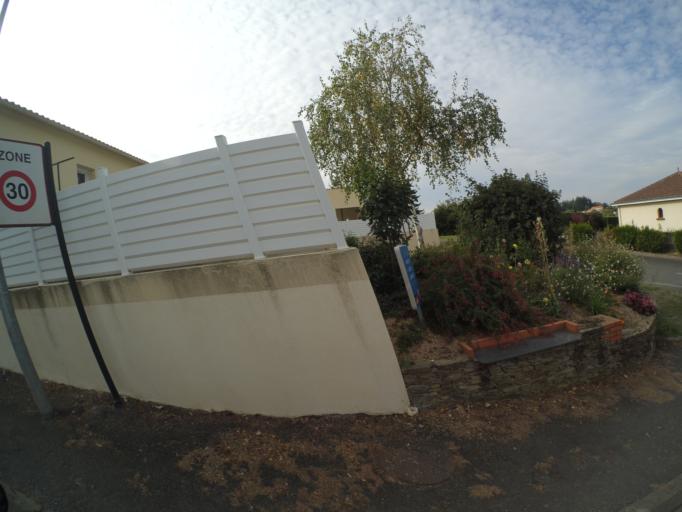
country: FR
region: Pays de la Loire
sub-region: Departement de Maine-et-Loire
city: Andreze
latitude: 47.1721
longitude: -0.9556
